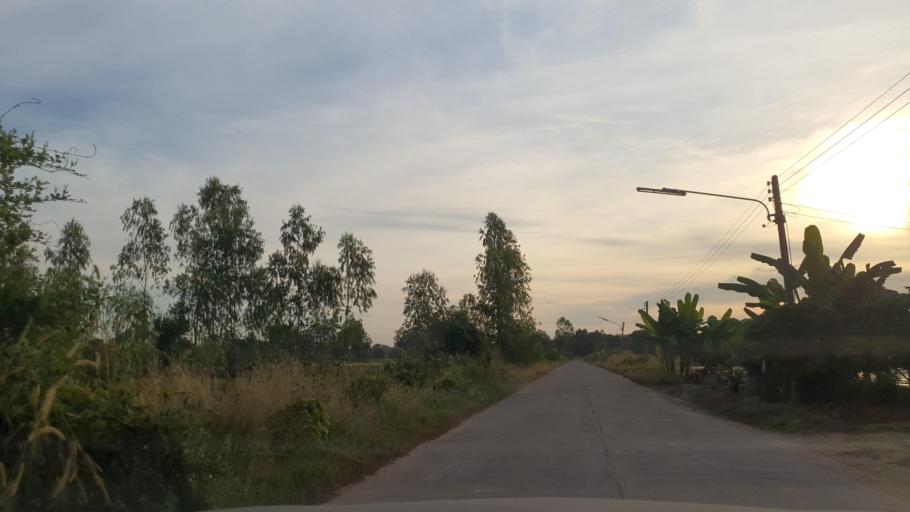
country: TH
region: Nakhon Sawan
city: Krok Phra
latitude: 15.6630
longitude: 100.0115
